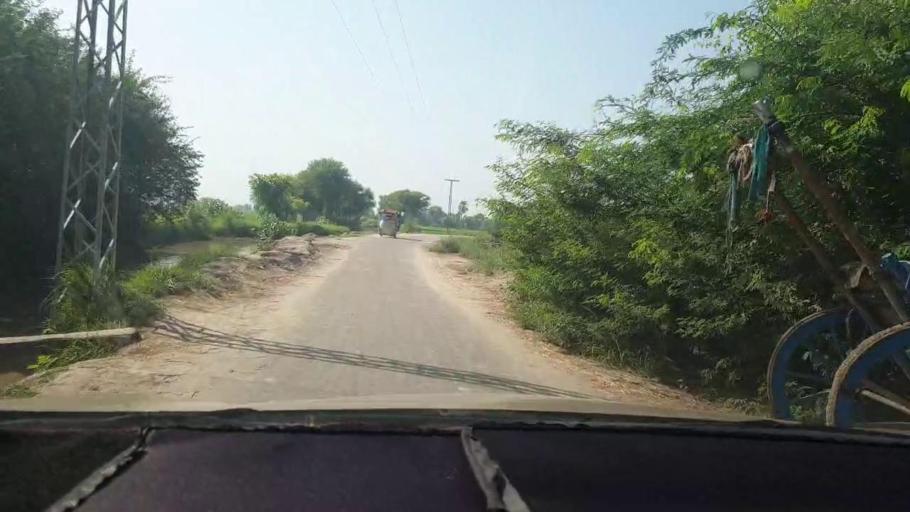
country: PK
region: Sindh
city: Kambar
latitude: 27.5753
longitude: 68.0753
